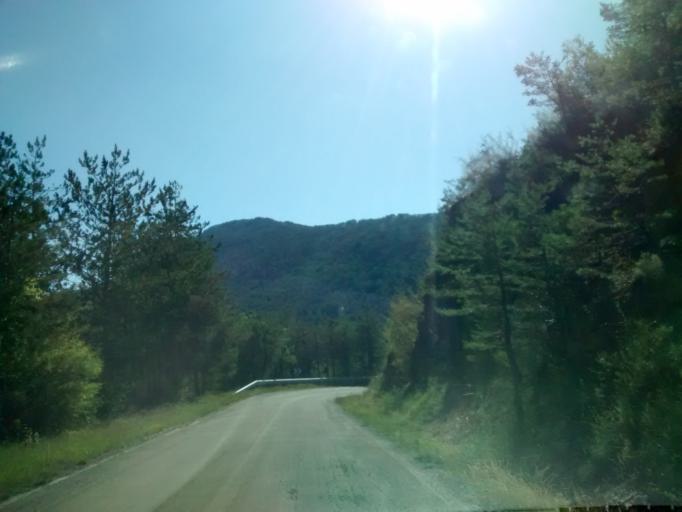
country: ES
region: Aragon
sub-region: Provincia de Huesca
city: Jaca
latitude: 42.4926
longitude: -0.5624
